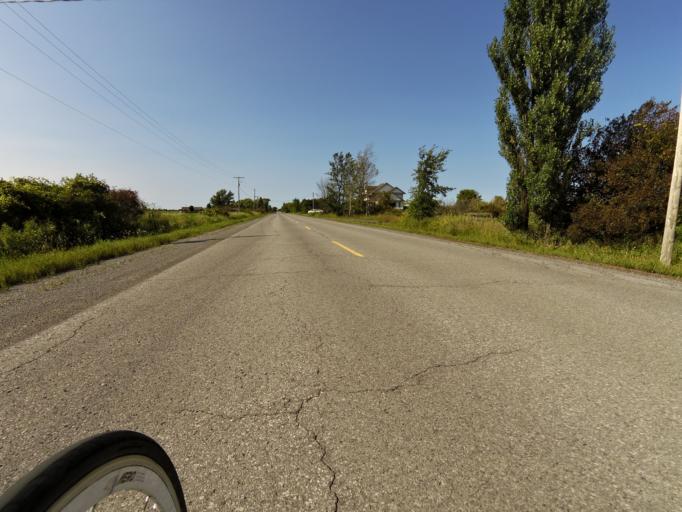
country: CA
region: Ontario
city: Carleton Place
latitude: 45.3344
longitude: -76.0934
